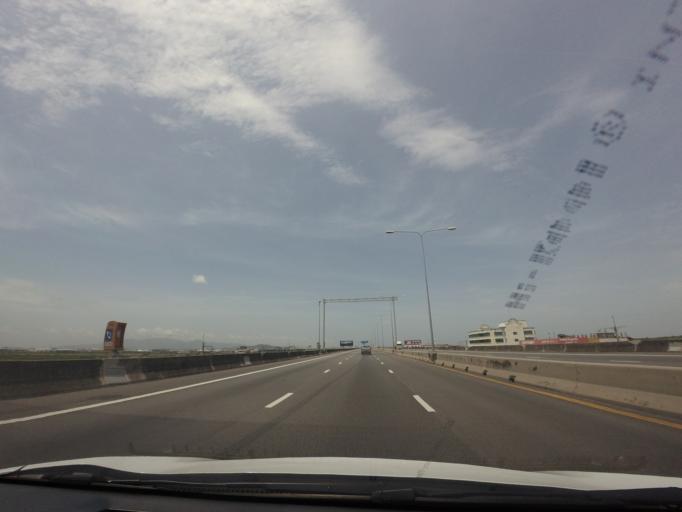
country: TH
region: Chachoengsao
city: Bang Pakong
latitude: 13.4699
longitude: 100.9971
